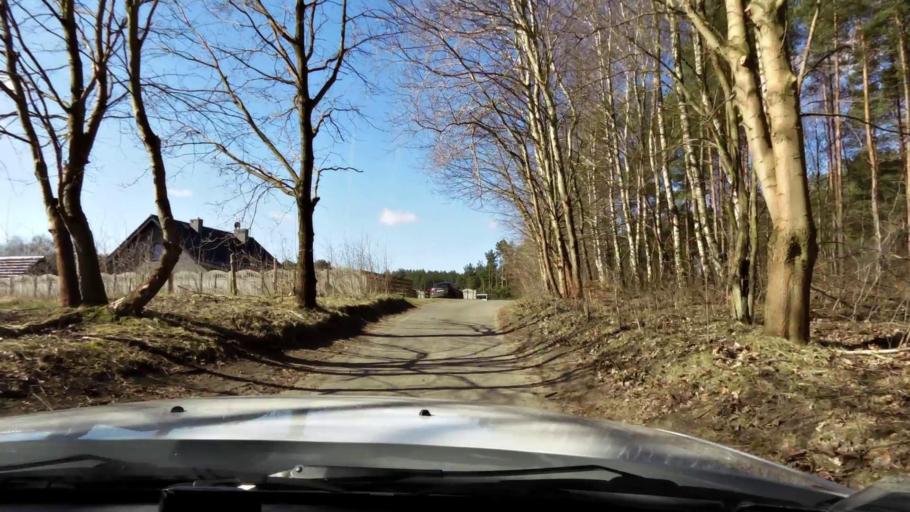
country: PL
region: West Pomeranian Voivodeship
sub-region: Powiat gryfinski
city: Gryfino
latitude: 53.2174
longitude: 14.5148
